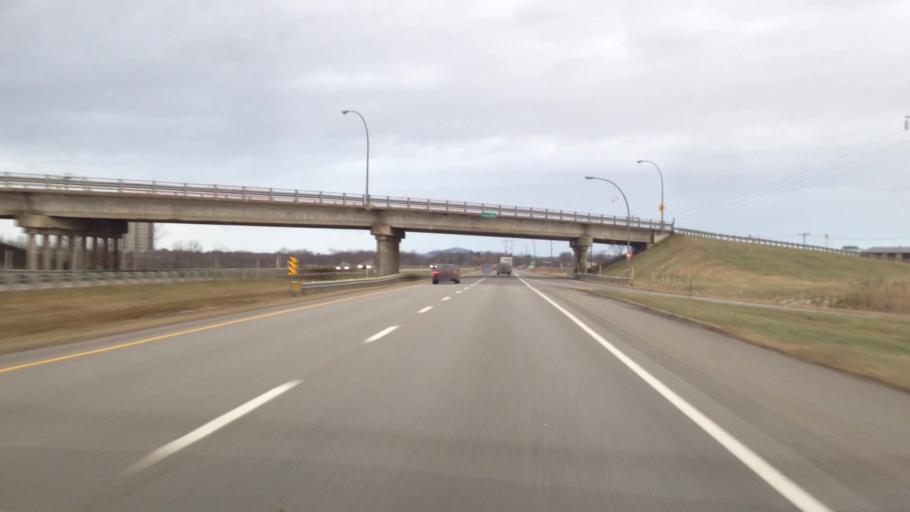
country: CA
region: Quebec
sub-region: Monteregie
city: Rigaud
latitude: 45.4879
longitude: -74.3145
